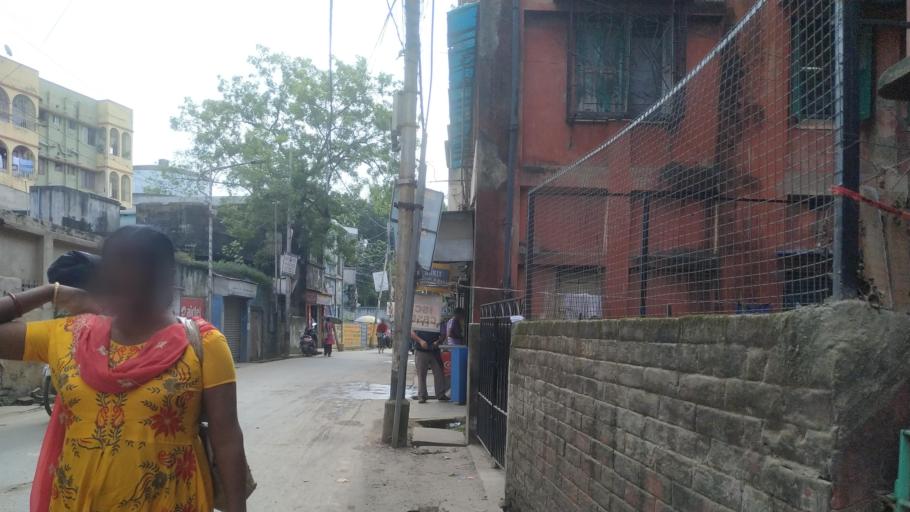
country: IN
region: West Bengal
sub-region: North 24 Parganas
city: Dam Dam
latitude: 22.6401
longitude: 88.4152
